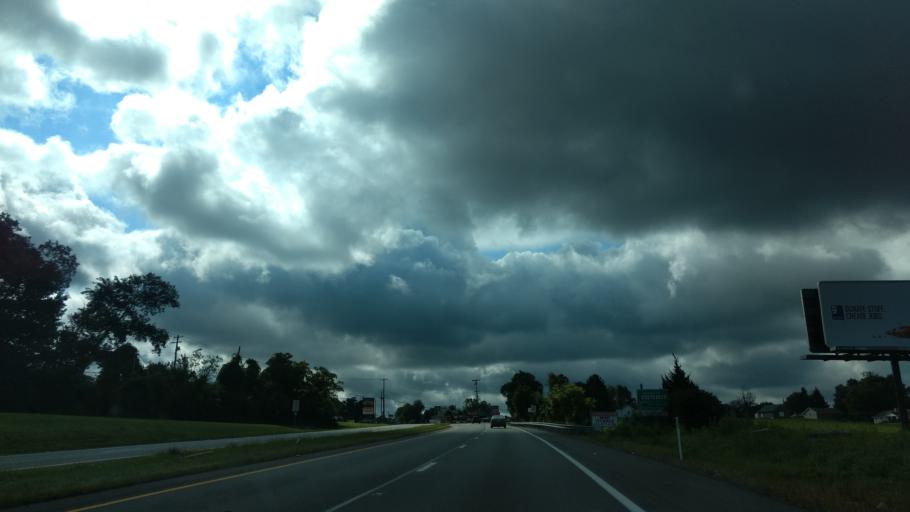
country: US
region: Pennsylvania
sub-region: Westmoreland County
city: Fellsburg
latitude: 40.2056
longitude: -79.8390
